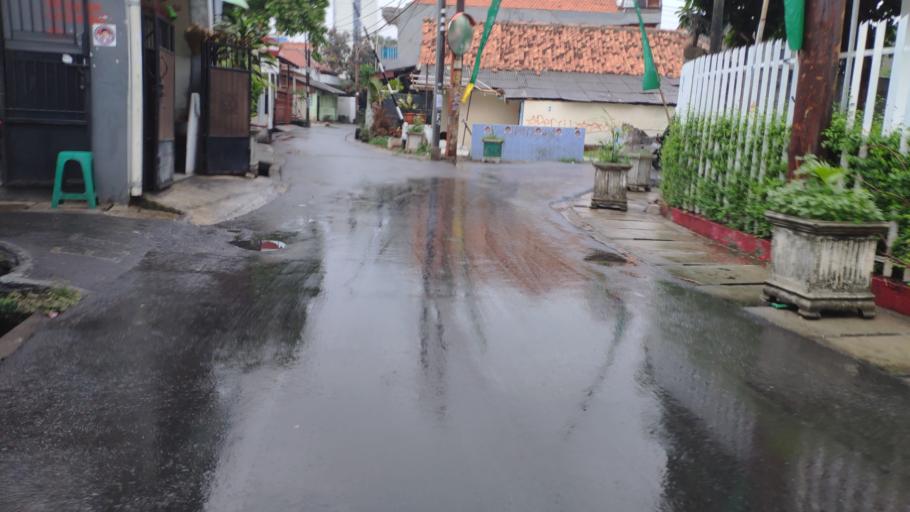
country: ID
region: Jakarta Raya
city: Jakarta
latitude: -6.2065
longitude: 106.8720
